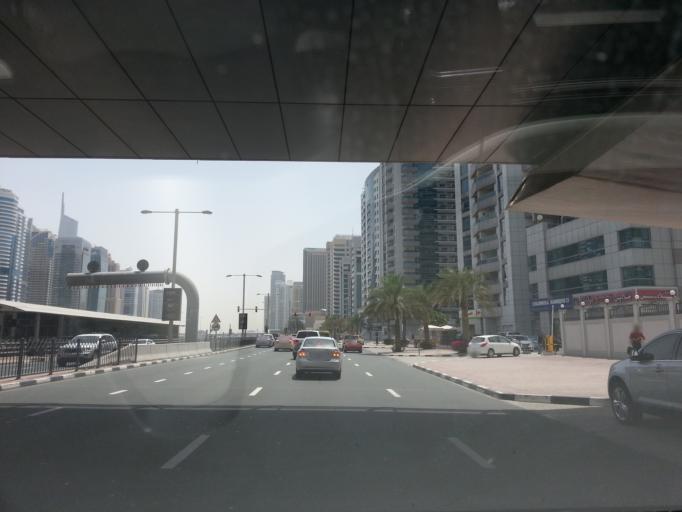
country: AE
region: Dubai
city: Dubai
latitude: 25.0815
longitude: 55.1473
